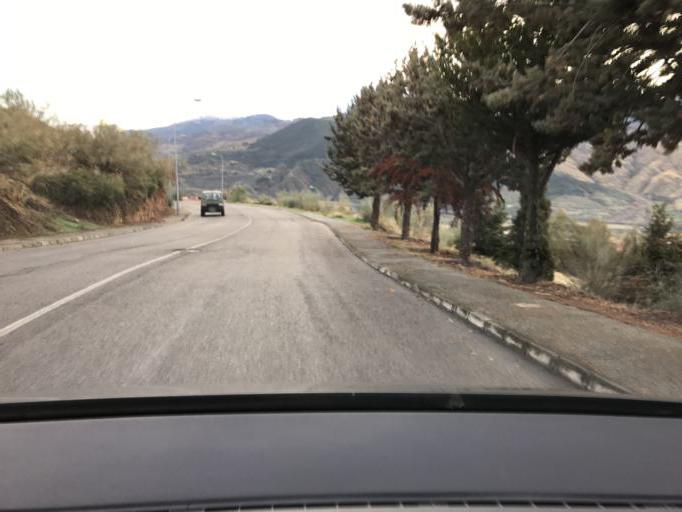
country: ES
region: Andalusia
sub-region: Provincia de Granada
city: Cenes de la Vega
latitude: 37.1670
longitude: -3.5432
